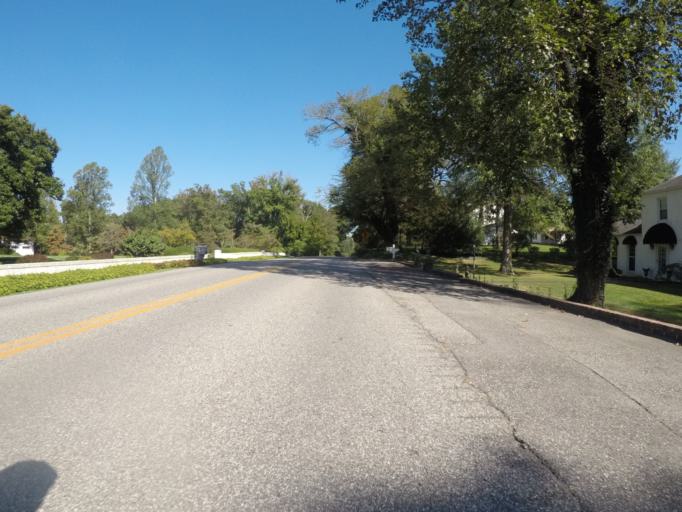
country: US
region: Kentucky
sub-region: Greenup County
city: Russell
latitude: 38.4954
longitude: -82.6955
